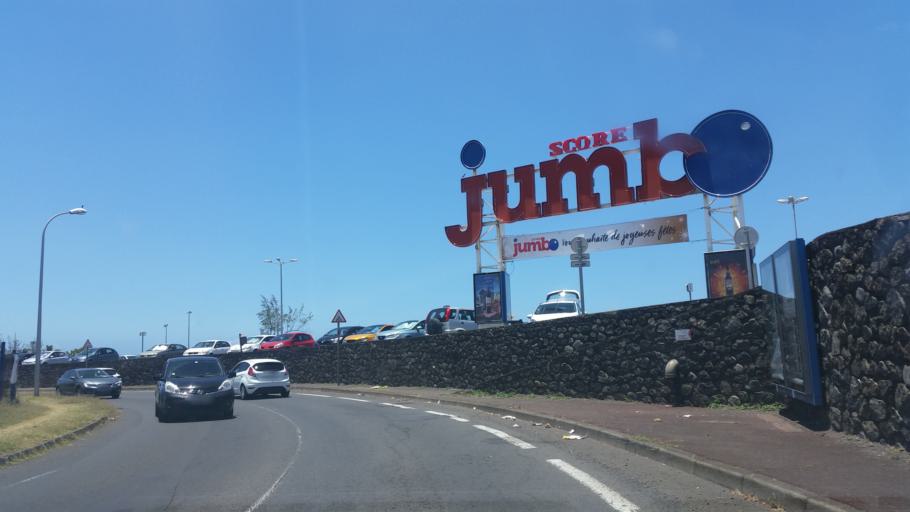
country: RE
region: Reunion
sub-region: Reunion
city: Saint-Pierre
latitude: -21.3354
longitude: 55.4562
